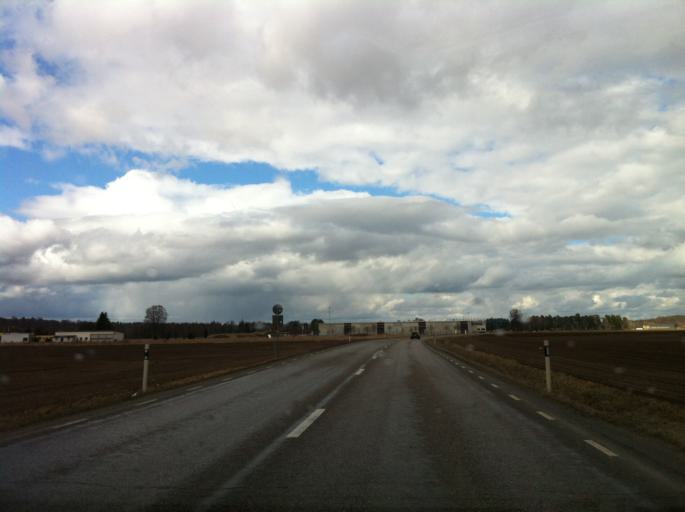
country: SE
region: Vaestra Goetaland
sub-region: Ulricehamns Kommun
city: Ulricehamn
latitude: 57.7628
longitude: 13.4059
